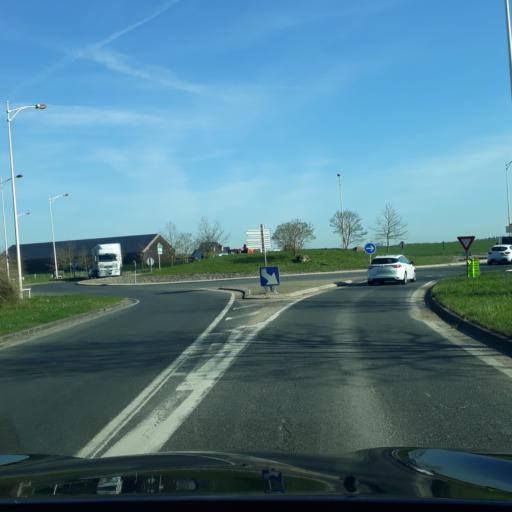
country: FR
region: Ile-de-France
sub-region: Departement de l'Essonne
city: Ballancourt-sur-Essonne
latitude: 48.5242
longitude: 2.3941
